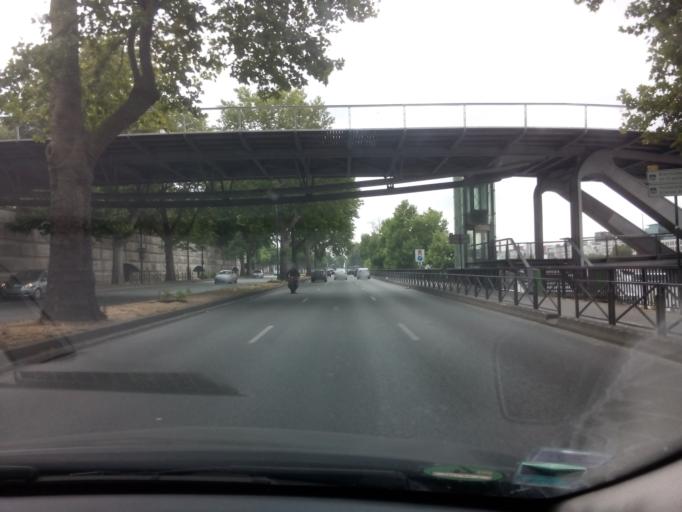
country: FR
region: Ile-de-France
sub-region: Departement du Val-de-Marne
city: Ivry-sur-Seine
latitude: 48.8361
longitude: 2.3788
